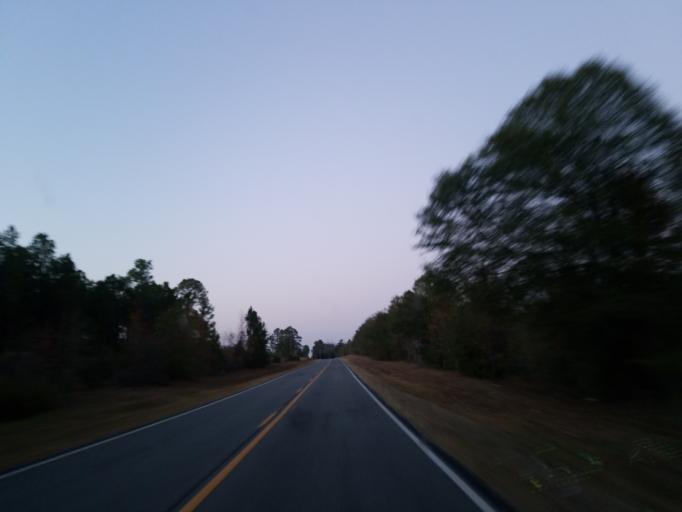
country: US
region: Georgia
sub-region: Wilcox County
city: Rochelle
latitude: 31.8409
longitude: -83.5630
